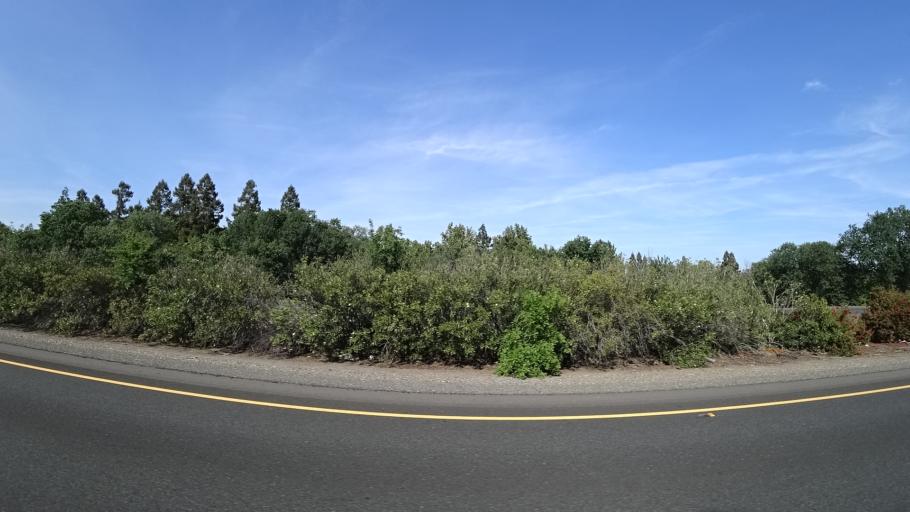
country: US
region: California
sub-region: Butte County
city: Chico
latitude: 39.7630
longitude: -121.8593
